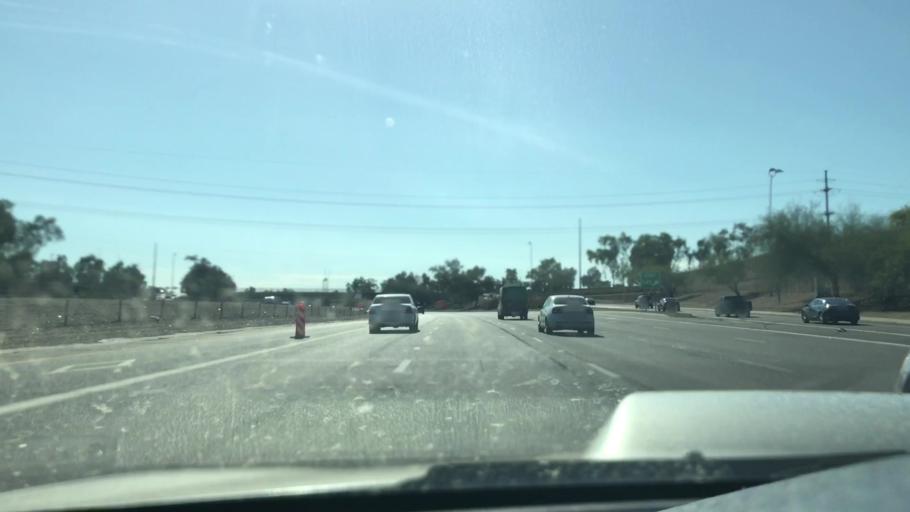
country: US
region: Arizona
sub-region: Maricopa County
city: Phoenix
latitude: 33.4618
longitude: -112.1331
